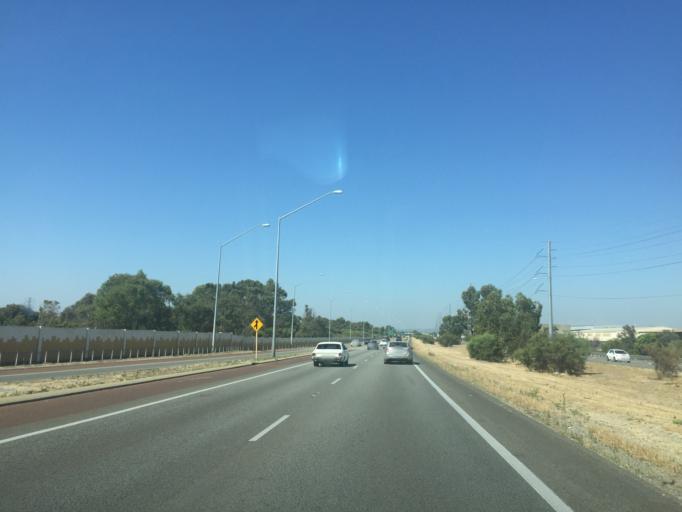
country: AU
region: Western Australia
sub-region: Canning
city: Willetton
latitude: -32.0662
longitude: 115.8932
